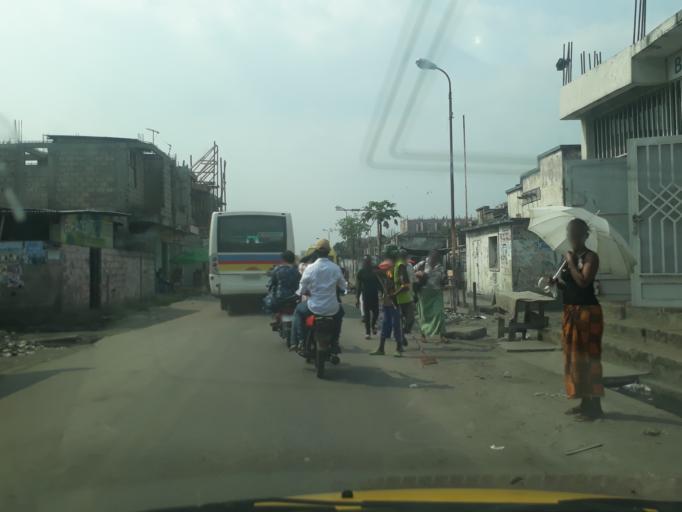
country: CD
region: Kinshasa
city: Kinshasa
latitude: -4.3188
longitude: 15.3203
